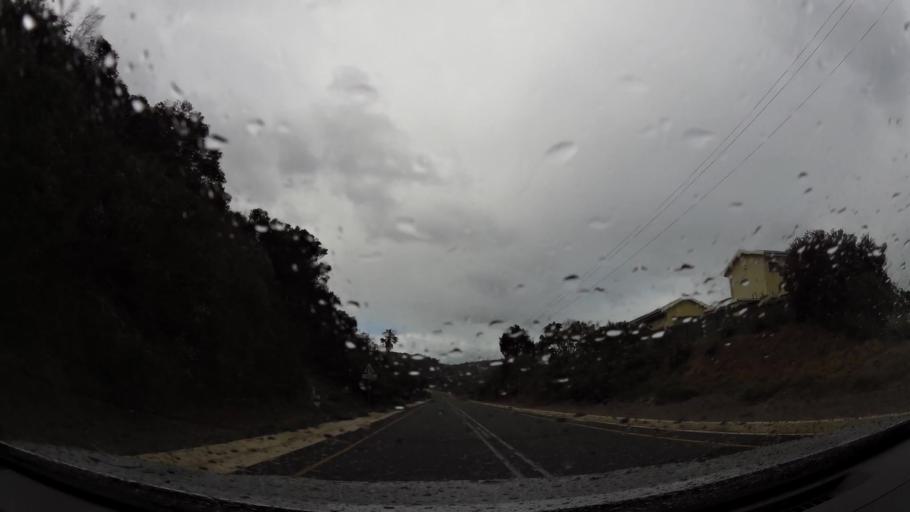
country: ZA
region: Western Cape
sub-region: Eden District Municipality
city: George
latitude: -34.0482
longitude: 22.3066
